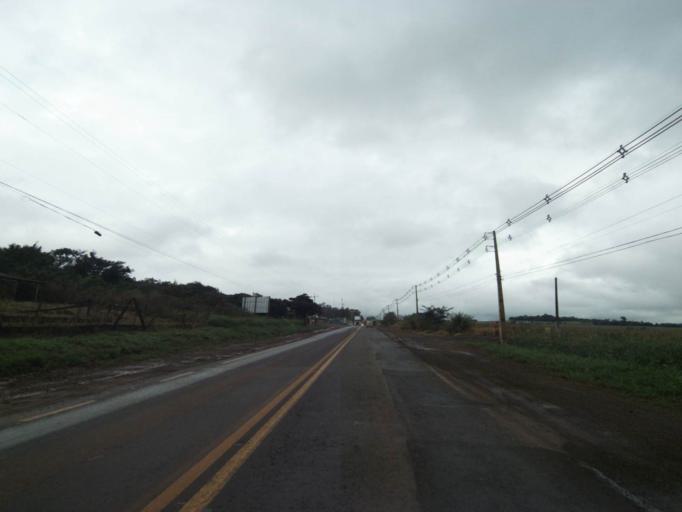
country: BR
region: Parana
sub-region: Marechal Candido Rondon
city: Marechal Candido Rondon
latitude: -24.5685
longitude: -54.0206
